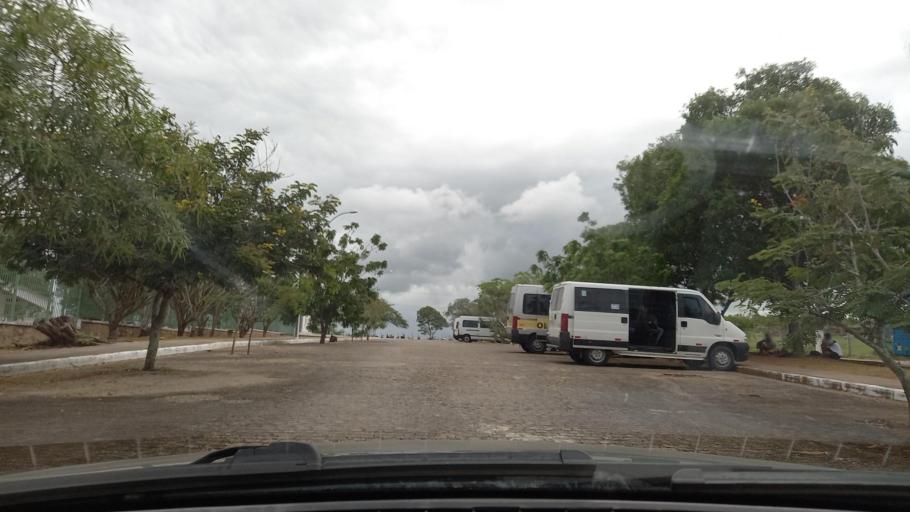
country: BR
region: Sergipe
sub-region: Caninde De Sao Francisco
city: Caninde de Sao Francisco
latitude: -9.6222
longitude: -37.7653
